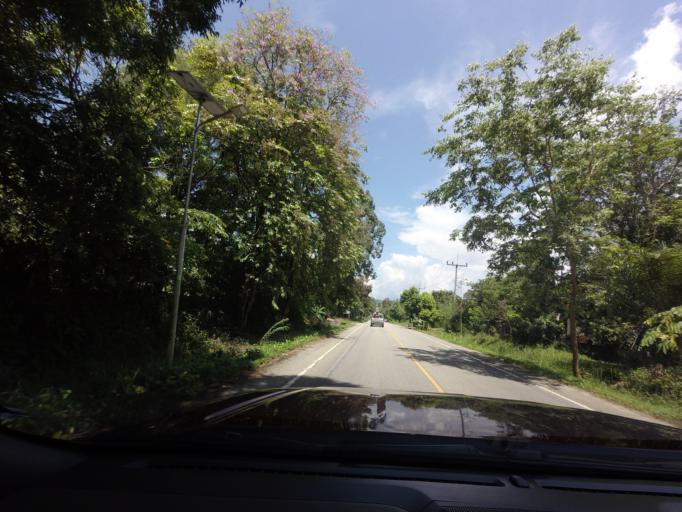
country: TH
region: Narathiwat
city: Chanae
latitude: 6.1369
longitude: 101.7005
